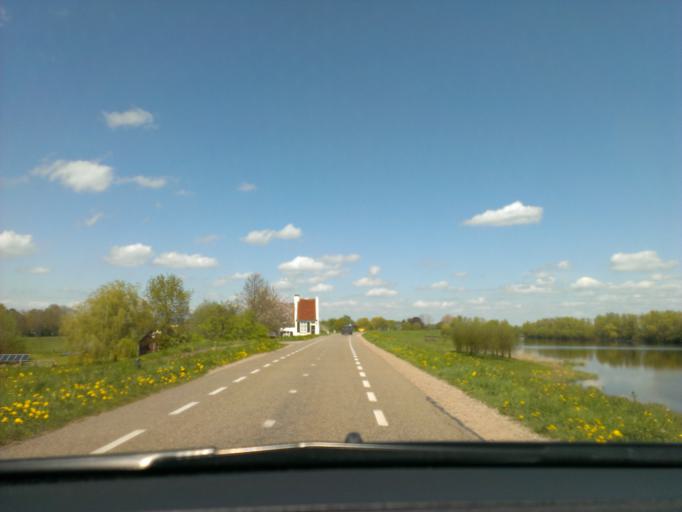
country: NL
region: Overijssel
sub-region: Gemeente Olst-Wijhe
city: Olst
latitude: 52.3277
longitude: 6.0880
